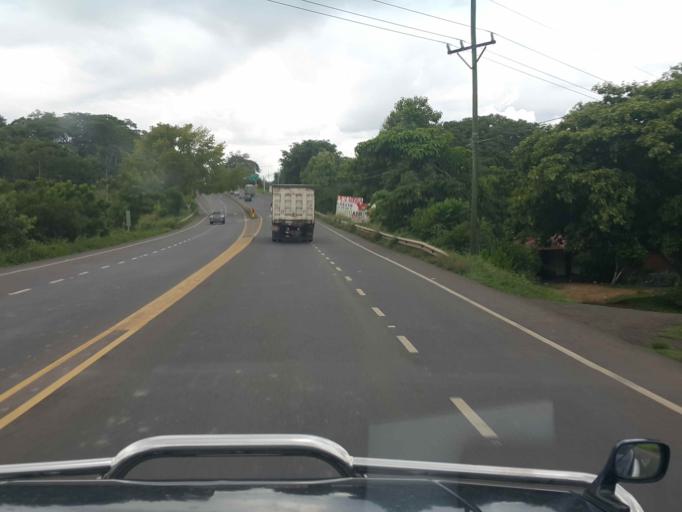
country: CR
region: Puntarenas
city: Esparza
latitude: 9.8928
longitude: -84.6493
